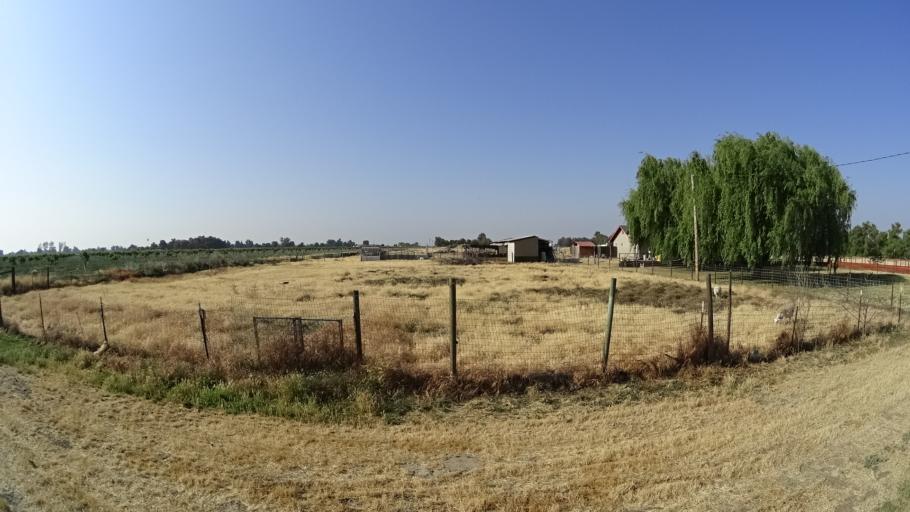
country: US
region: California
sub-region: Fresno County
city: Riverdale
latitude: 36.3584
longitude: -119.8652
